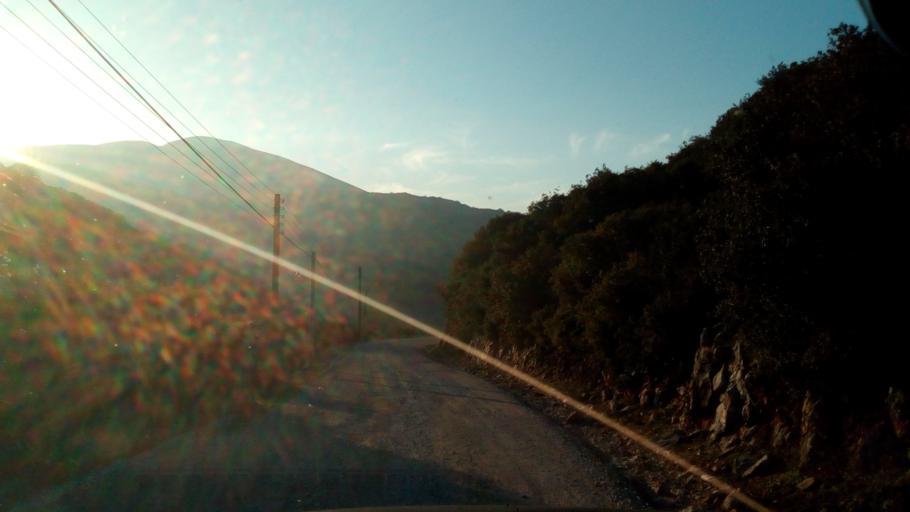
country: GR
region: West Greece
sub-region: Nomos Aitolias kai Akarnanias
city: Nafpaktos
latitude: 38.4687
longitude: 21.8221
